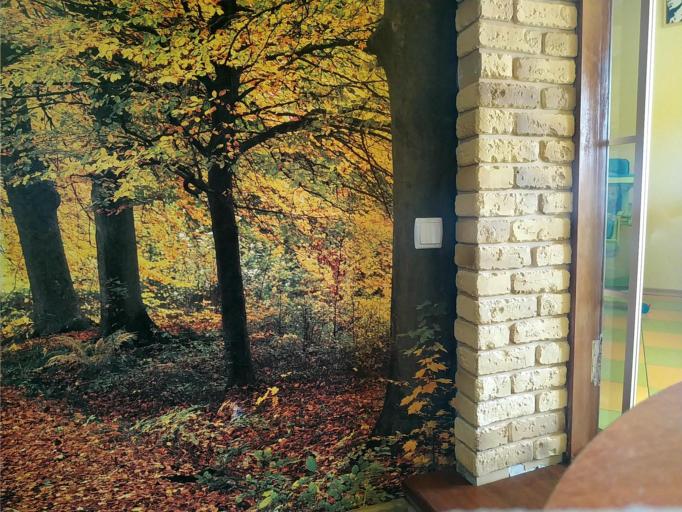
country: RU
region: Smolensk
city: Katyn'
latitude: 54.9480
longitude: 31.7127
